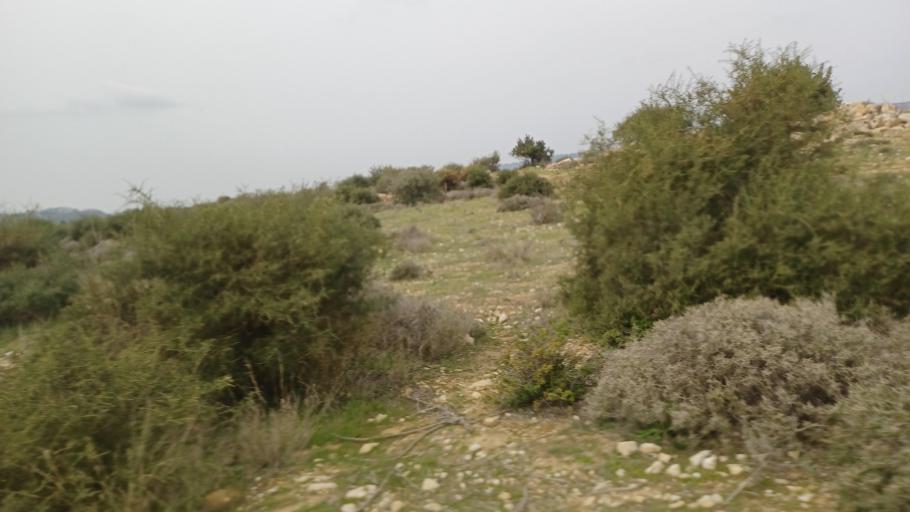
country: CY
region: Limassol
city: Pachna
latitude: 34.7533
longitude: 32.7397
